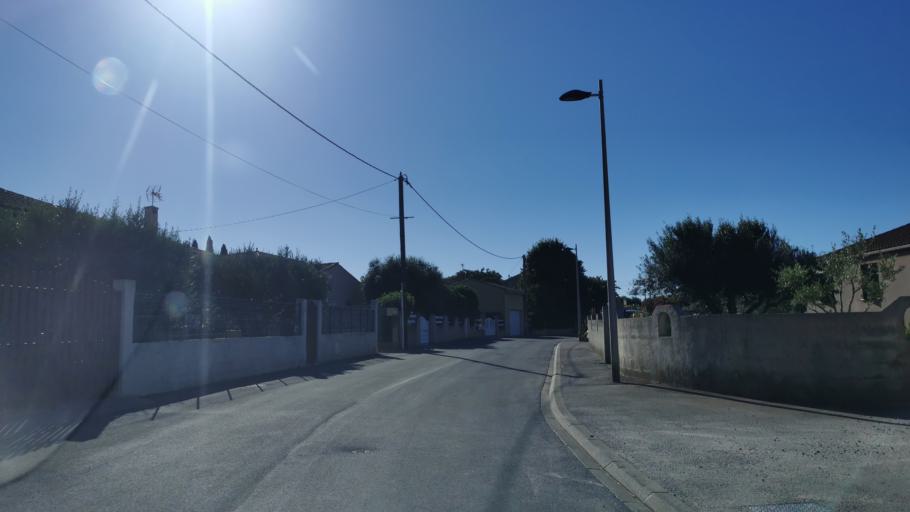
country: FR
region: Languedoc-Roussillon
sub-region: Departement de l'Aude
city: Coursan
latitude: 43.2361
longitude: 3.0661
